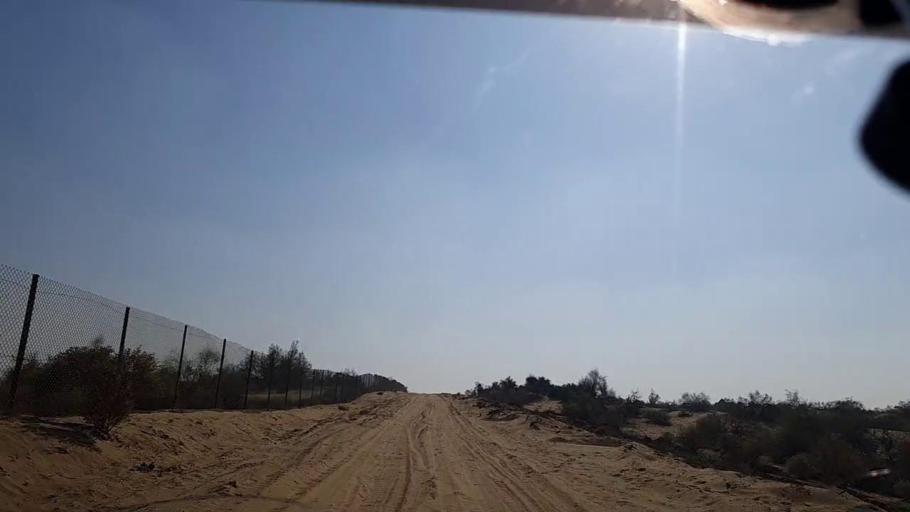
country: PK
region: Sindh
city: Khanpur
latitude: 27.5639
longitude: 69.3888
